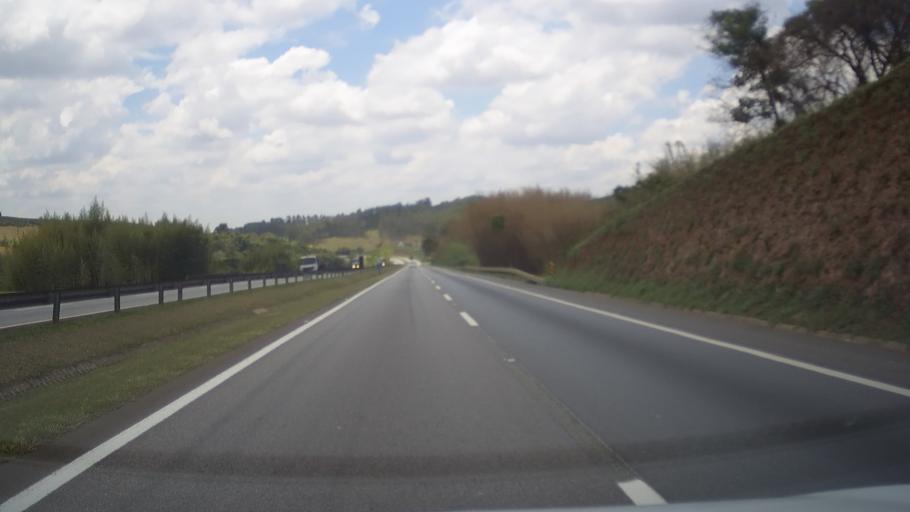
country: BR
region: Minas Gerais
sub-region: Tres Coracoes
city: Tres Coracoes
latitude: -21.6964
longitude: -45.3621
